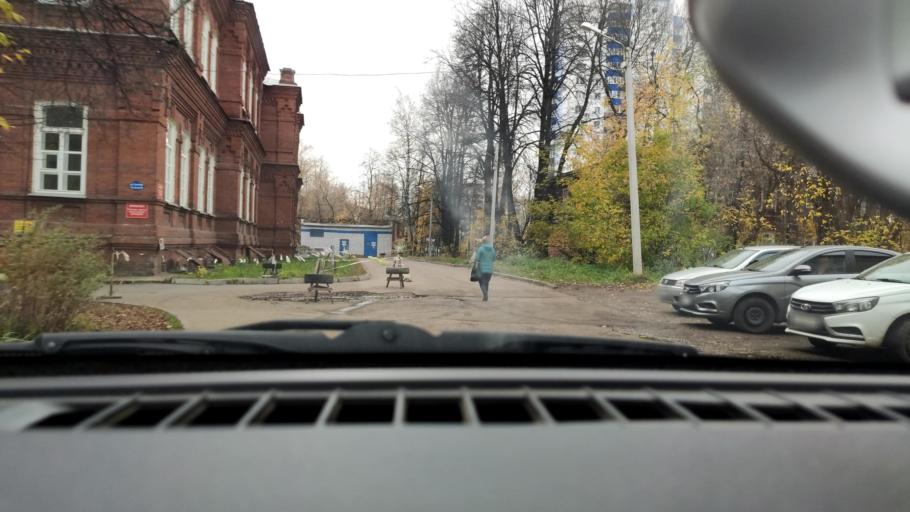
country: RU
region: Perm
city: Perm
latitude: 58.0277
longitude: 56.3044
